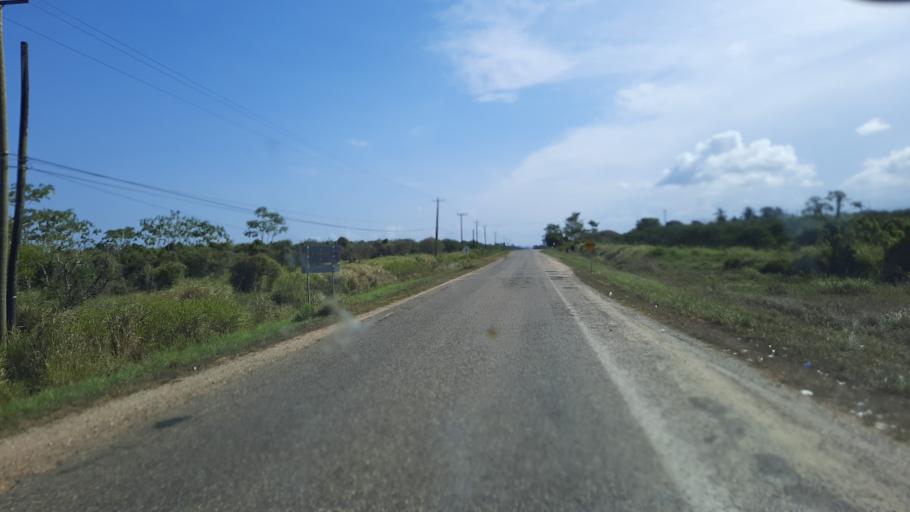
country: BZ
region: Stann Creek
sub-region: Dangriga
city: Dangriga
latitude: 16.9795
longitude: -88.2959
